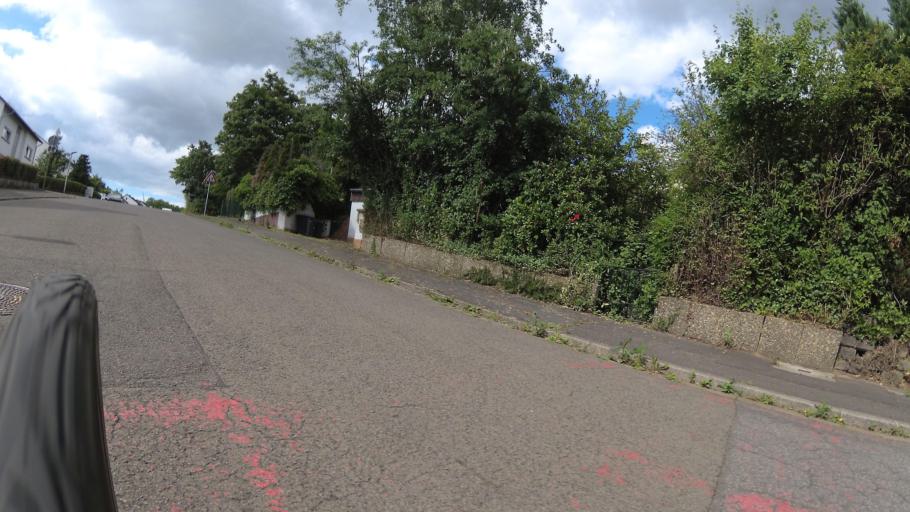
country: DE
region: Saarland
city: Volklingen
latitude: 49.2564
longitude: 6.8657
